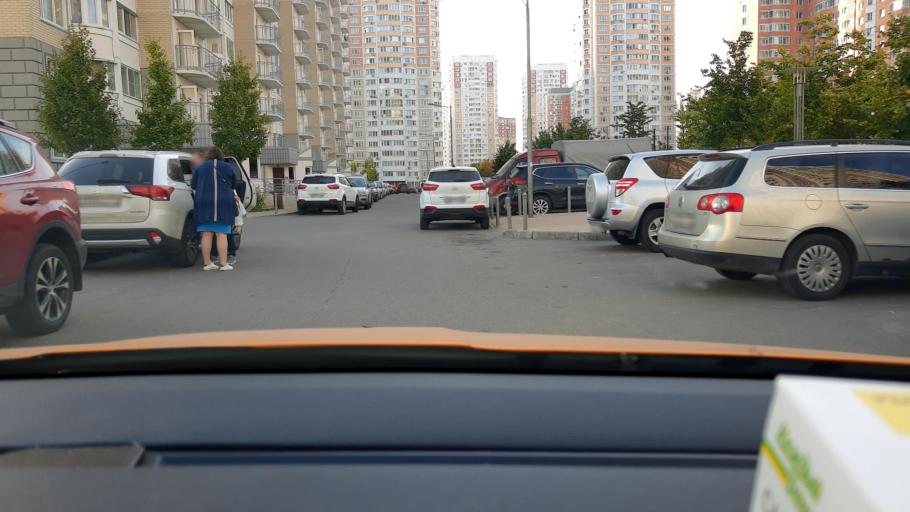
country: RU
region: Moskovskaya
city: Moskovskiy
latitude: 55.6015
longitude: 37.3650
